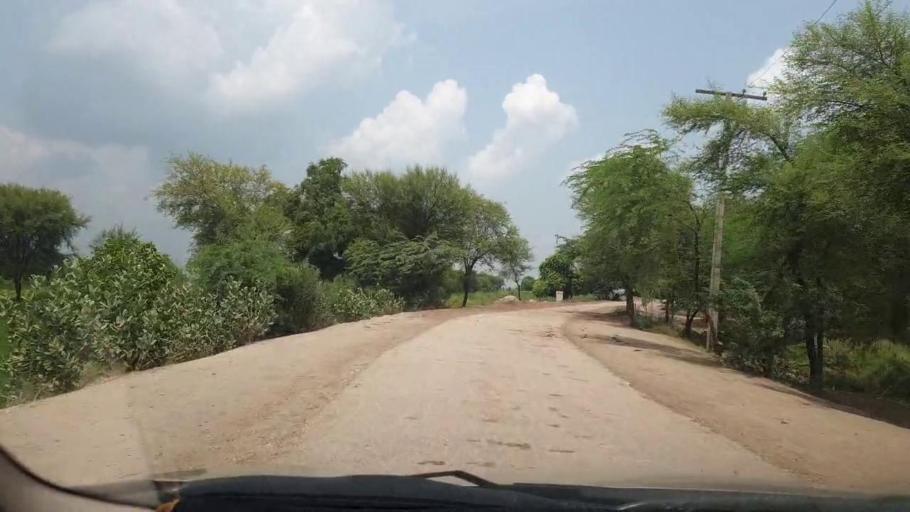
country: PK
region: Sindh
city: Larkana
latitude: 27.5973
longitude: 68.1398
